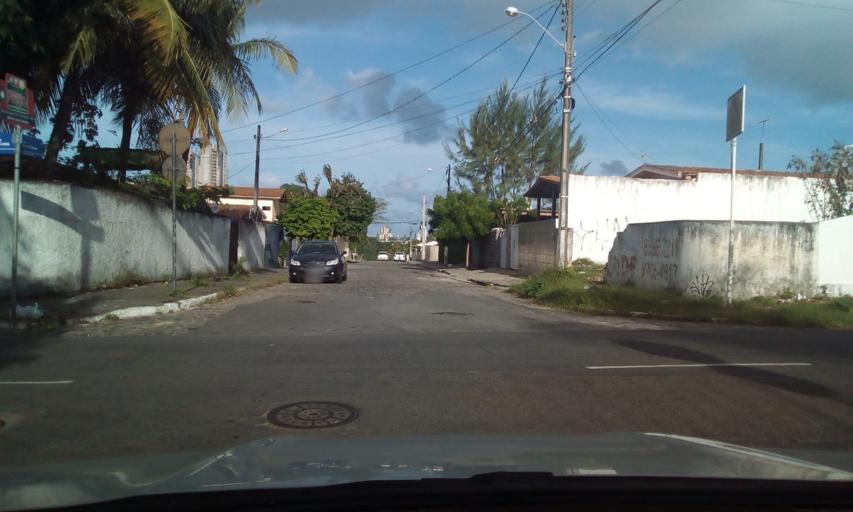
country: BR
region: Paraiba
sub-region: Joao Pessoa
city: Joao Pessoa
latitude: -7.1069
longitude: -34.8553
